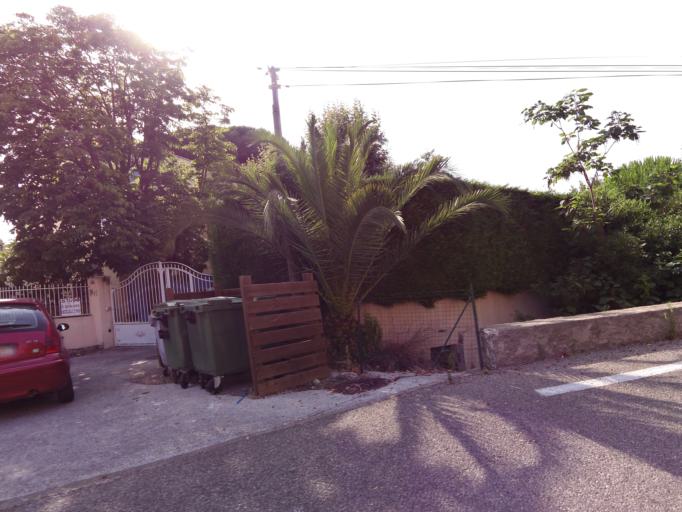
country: FR
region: Provence-Alpes-Cote d'Azur
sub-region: Departement du Var
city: Carqueiranne
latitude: 43.0901
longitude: 6.0760
